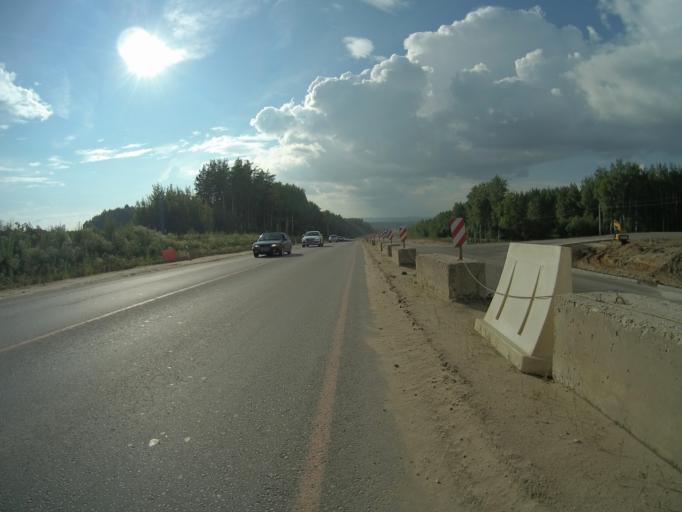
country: RU
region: Vladimir
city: Kommunar
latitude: 56.0725
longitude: 40.4897
